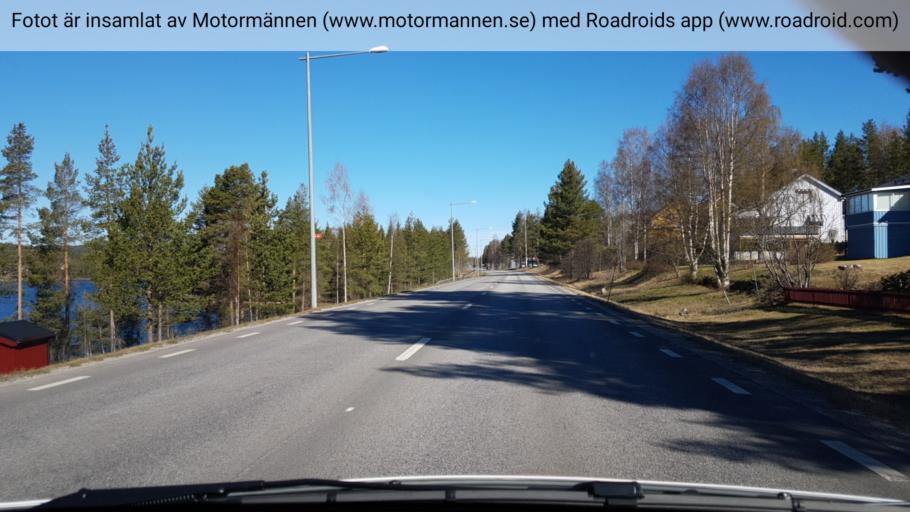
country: SE
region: Vaesterbotten
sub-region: Lycksele Kommun
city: Lycksele
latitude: 64.5775
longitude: 18.7071
